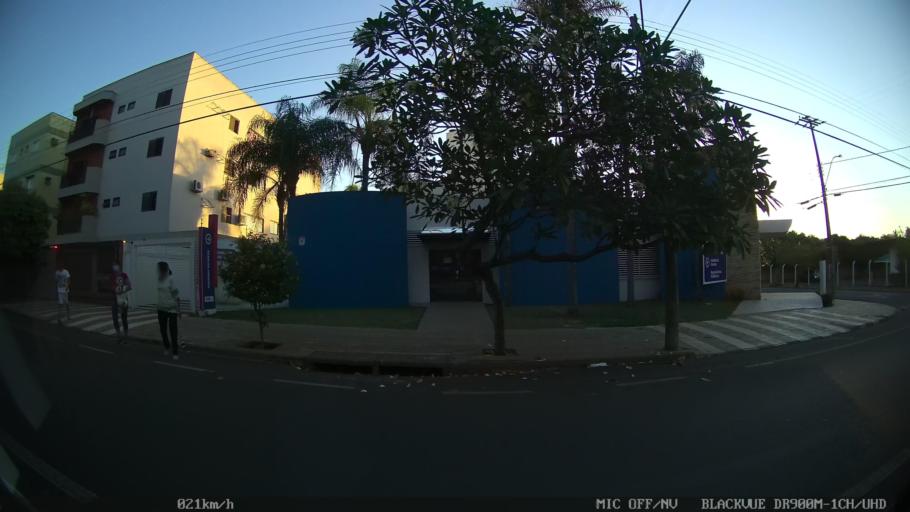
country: BR
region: Sao Paulo
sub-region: Sao Jose Do Rio Preto
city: Sao Jose do Rio Preto
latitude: -20.8480
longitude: -49.3941
